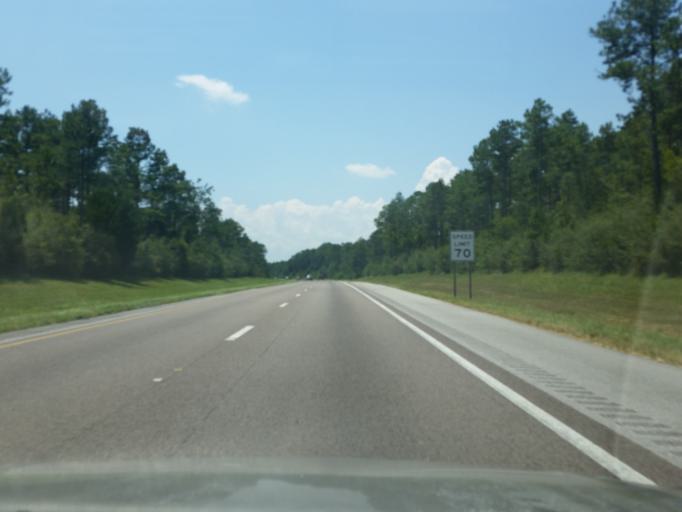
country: US
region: Florida
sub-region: Escambia County
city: Cantonment
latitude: 30.5804
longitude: -87.4800
